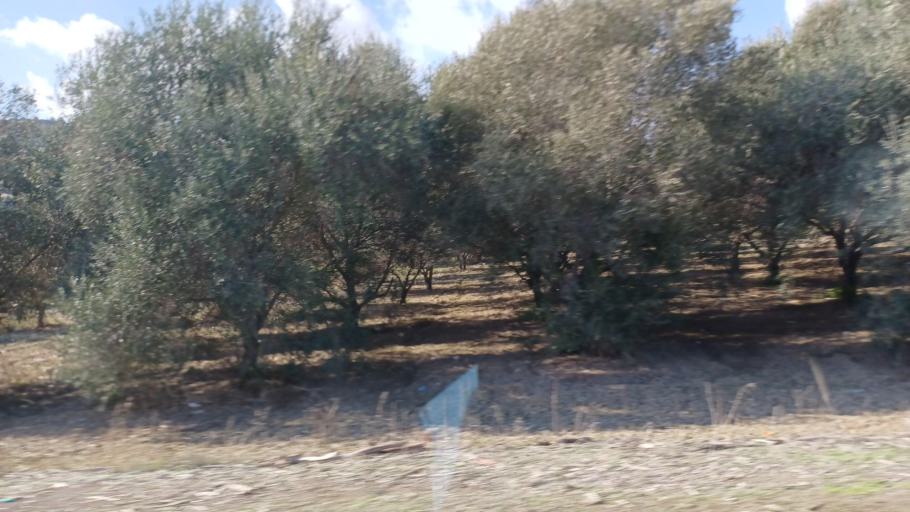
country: CY
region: Larnaka
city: Voroklini
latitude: 35.0005
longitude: 33.6530
